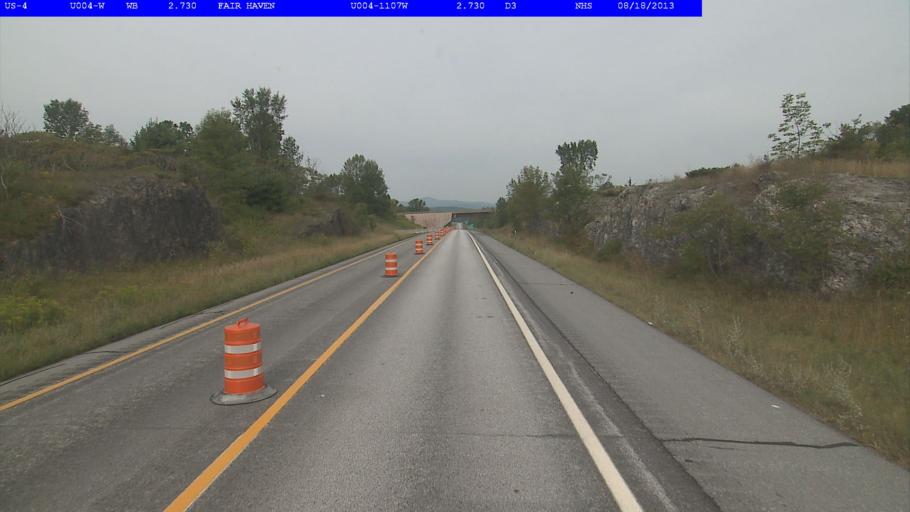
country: US
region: Vermont
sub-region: Rutland County
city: Fair Haven
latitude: 43.6056
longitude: -73.2567
